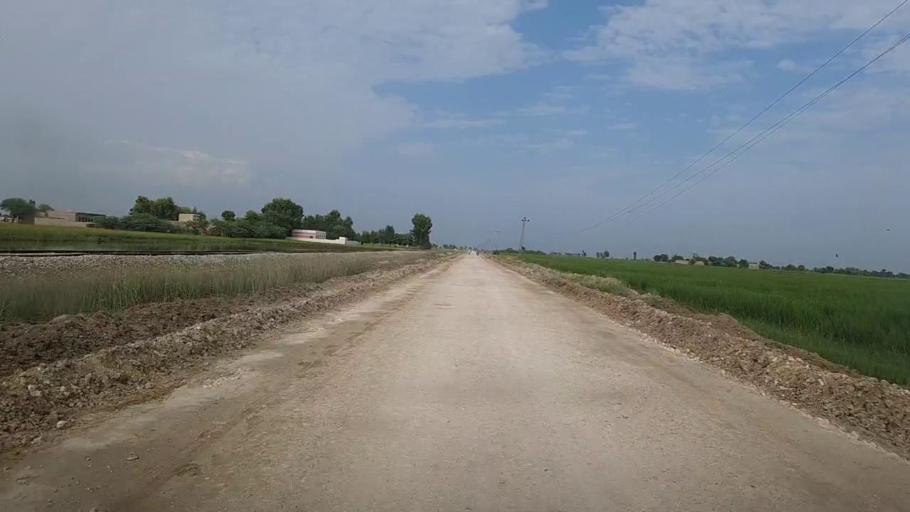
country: PK
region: Sindh
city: Thul
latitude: 28.2588
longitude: 68.8122
